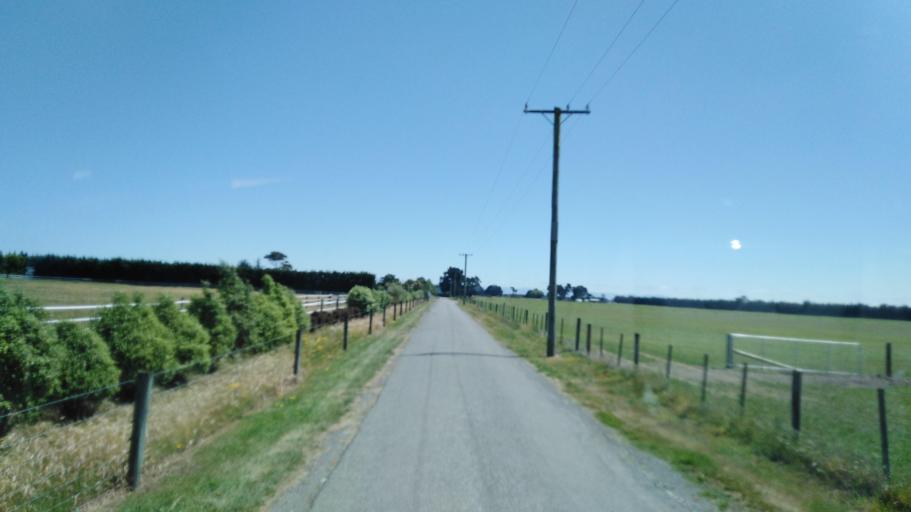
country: NZ
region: Canterbury
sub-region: Selwyn District
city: Rolleston
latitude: -43.5648
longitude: 172.4389
